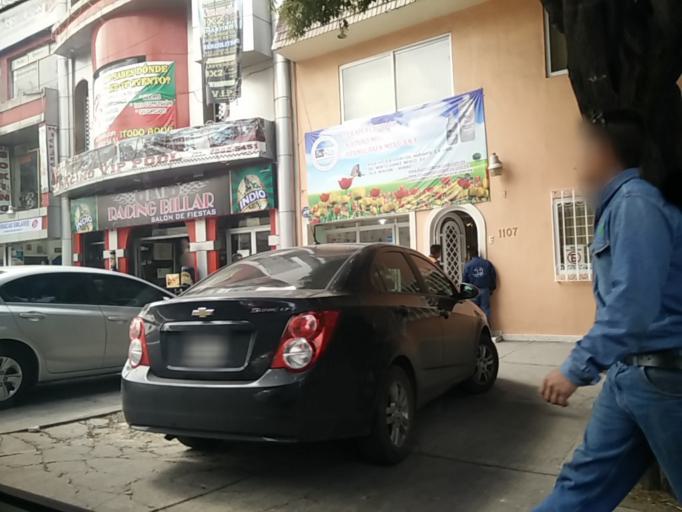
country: MX
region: Mexico City
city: Benito Juarez
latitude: 19.3959
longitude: -99.1581
